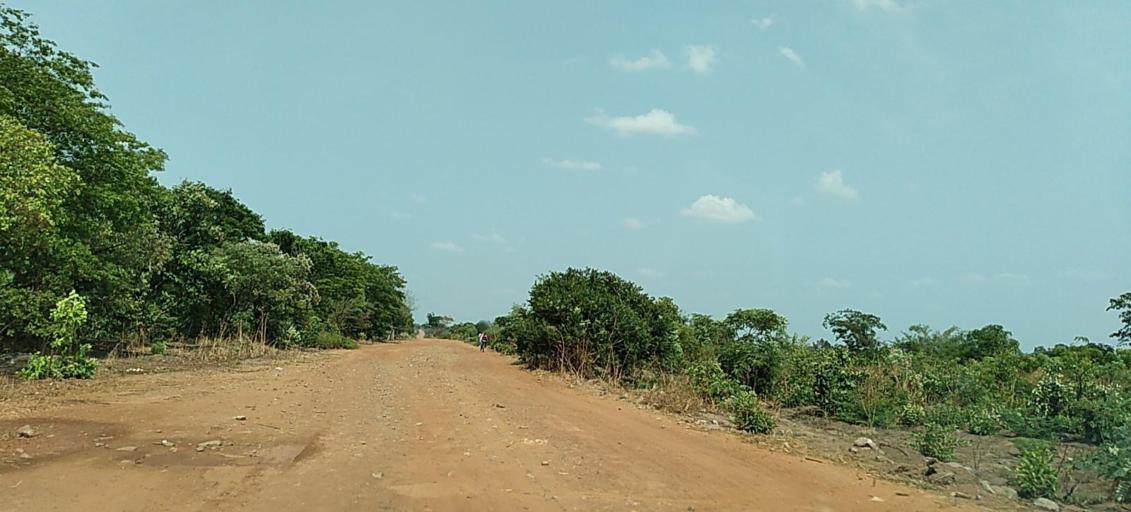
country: ZM
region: Copperbelt
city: Luanshya
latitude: -13.0923
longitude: 28.3039
